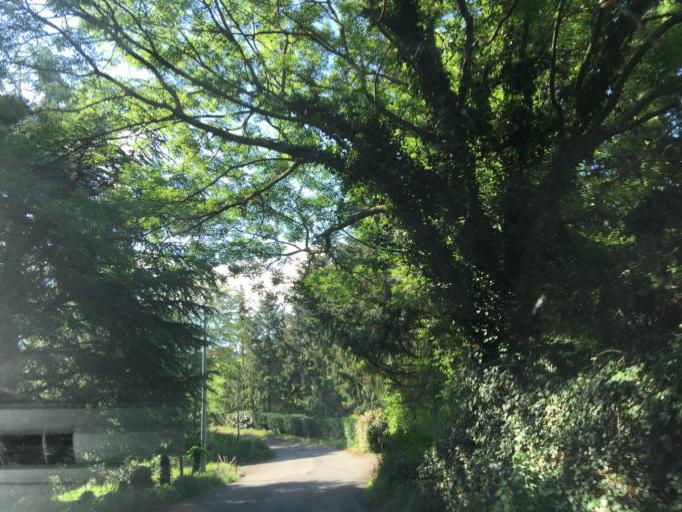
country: FR
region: Rhone-Alpes
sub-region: Departement de la Loire
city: Saint-Chamond
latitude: 45.4643
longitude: 4.5363
